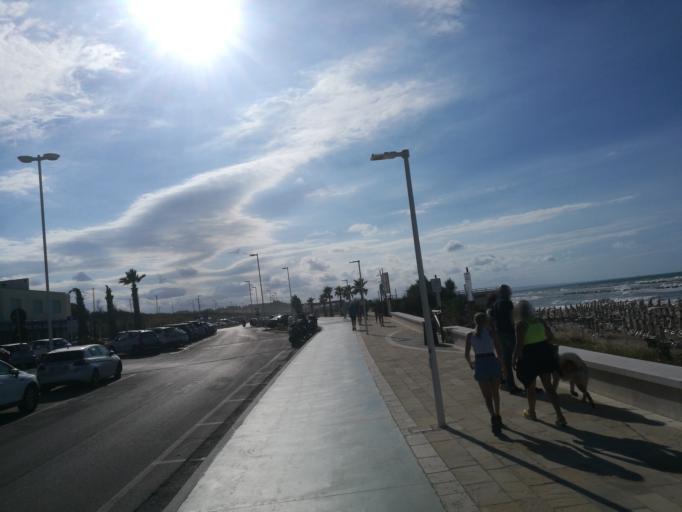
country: IT
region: Molise
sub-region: Provincia di Campobasso
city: Termoli
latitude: 42.0070
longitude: 14.9741
